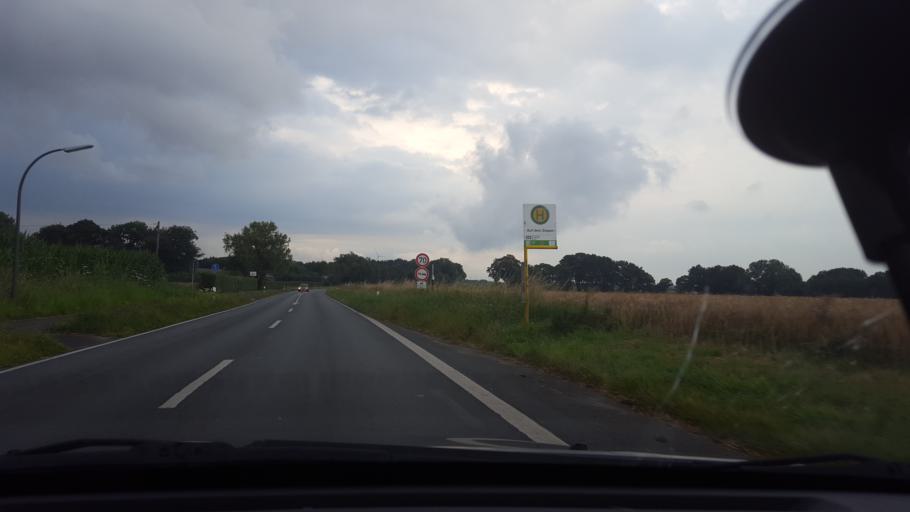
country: DE
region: North Rhine-Westphalia
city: Herten
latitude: 51.6353
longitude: 7.1560
